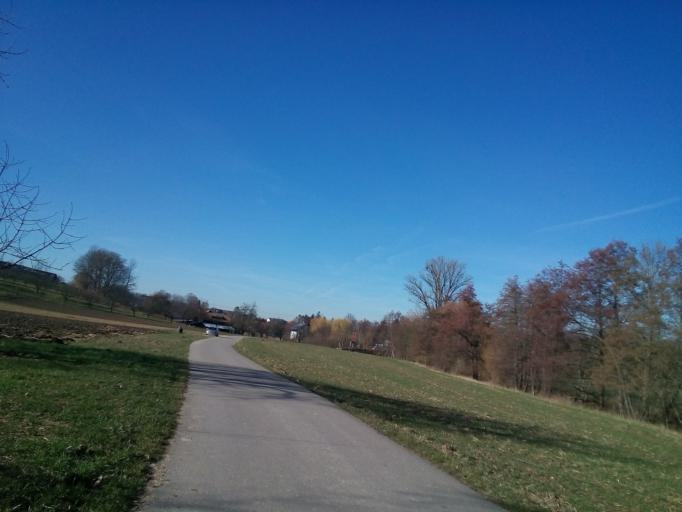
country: DE
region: Baden-Wuerttemberg
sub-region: Freiburg Region
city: Achern
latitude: 48.6114
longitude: 8.0645
